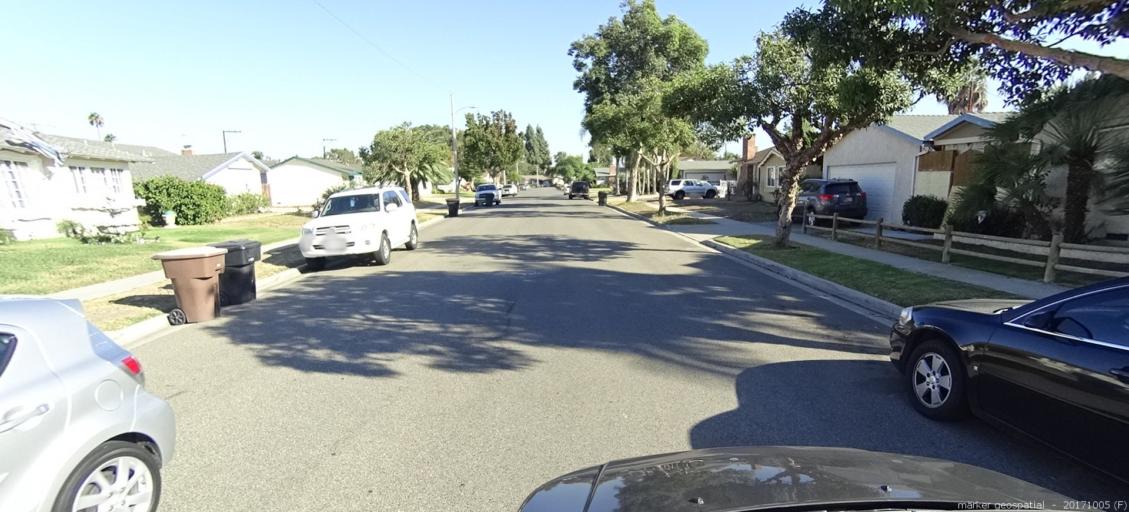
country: US
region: California
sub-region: Orange County
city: Stanton
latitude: 33.7934
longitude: -117.9741
